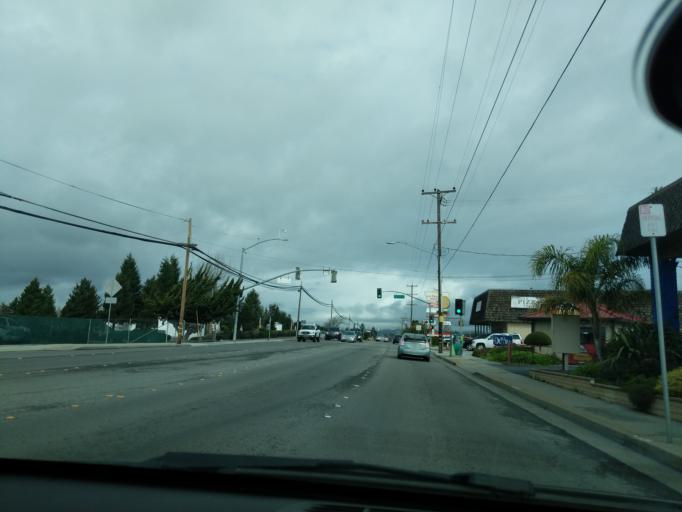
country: US
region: California
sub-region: Santa Cruz County
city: Freedom
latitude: 36.9246
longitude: -121.7628
